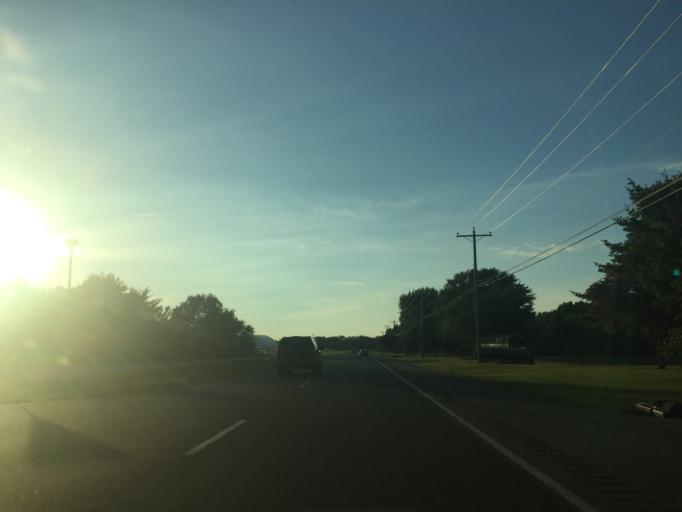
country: US
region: Delaware
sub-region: Kent County
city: Clayton
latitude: 39.3427
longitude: -75.6356
